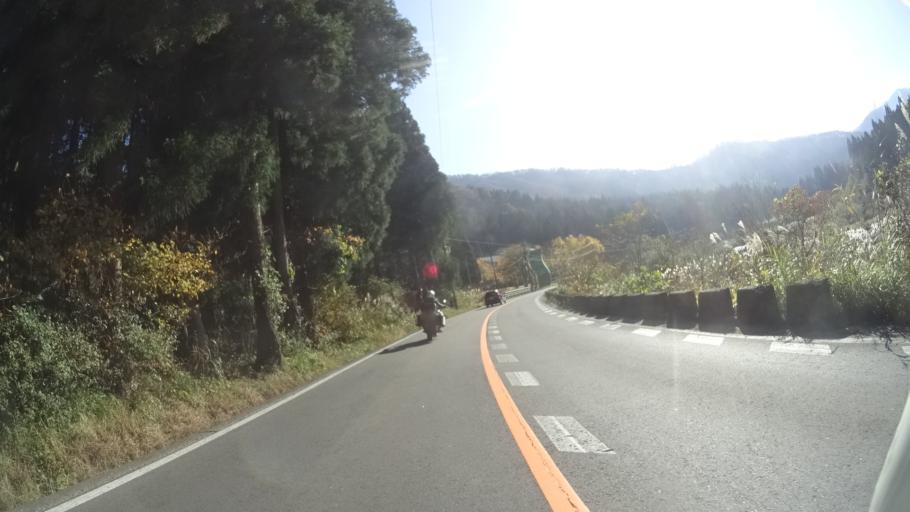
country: JP
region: Fukui
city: Ono
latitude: 35.9243
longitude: 136.6453
